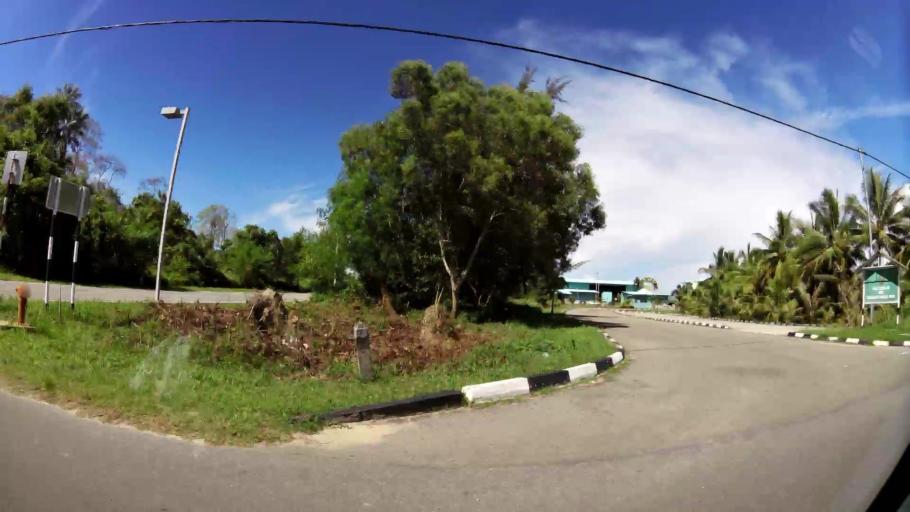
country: BN
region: Brunei and Muara
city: Bandar Seri Begawan
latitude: 5.0023
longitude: 115.0627
